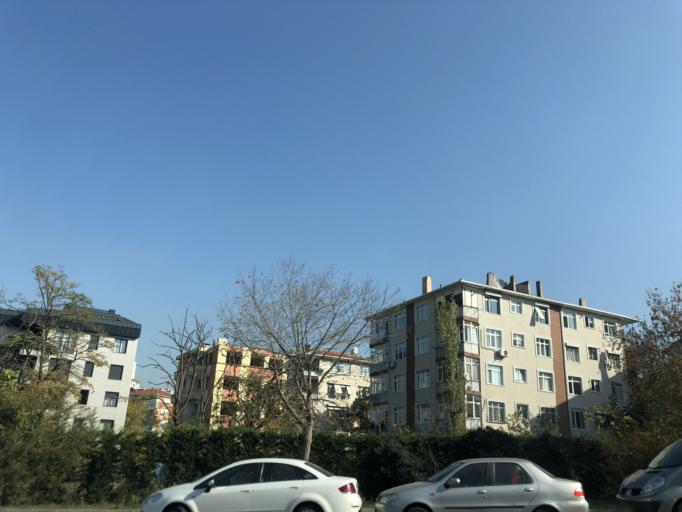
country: TR
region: Istanbul
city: UEskuedar
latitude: 40.9967
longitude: 29.0315
